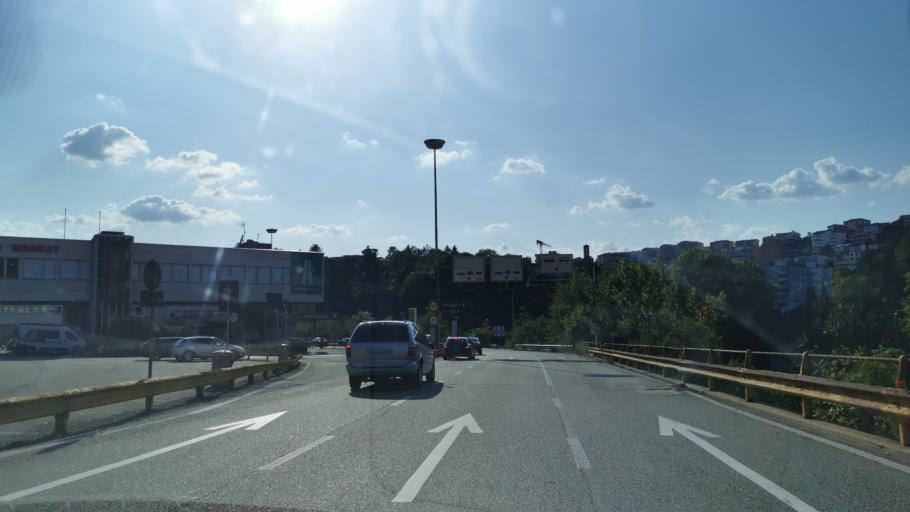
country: IT
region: Lombardy
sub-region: Provincia di Como
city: Maslianico
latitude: 45.8415
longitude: 9.0394
